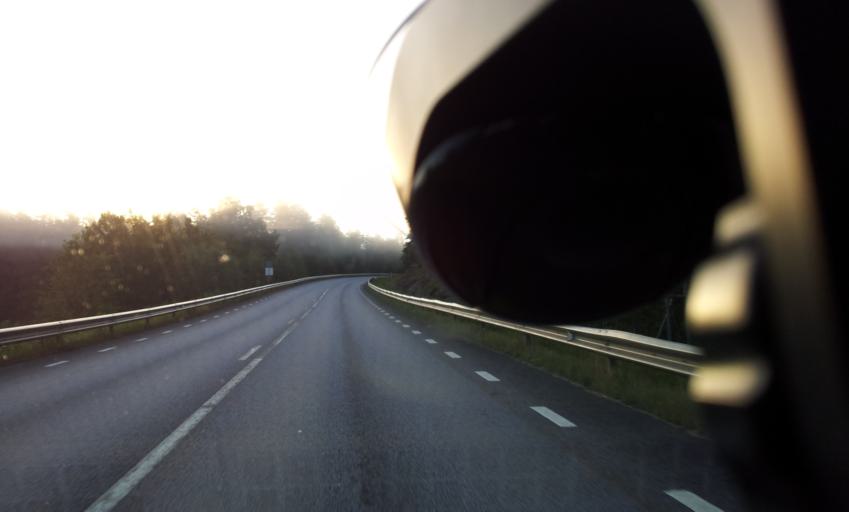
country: SE
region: Kalmar
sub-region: Vasterviks Kommun
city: Vaestervik
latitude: 57.7224
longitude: 16.4783
